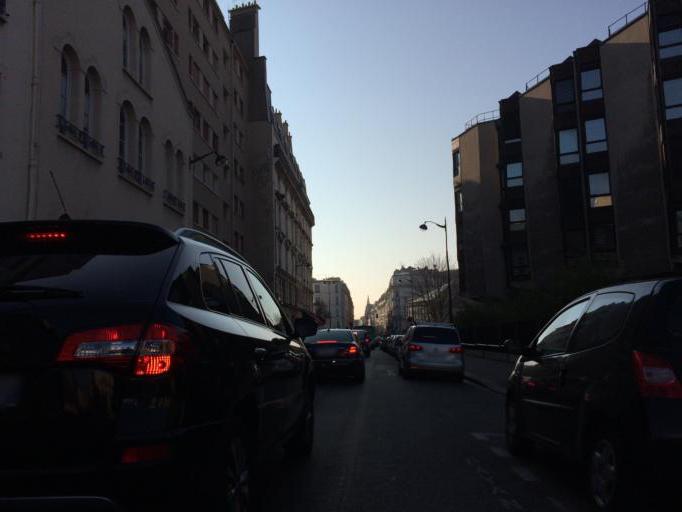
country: FR
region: Ile-de-France
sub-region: Paris
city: Paris
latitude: 48.8748
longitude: 2.3695
